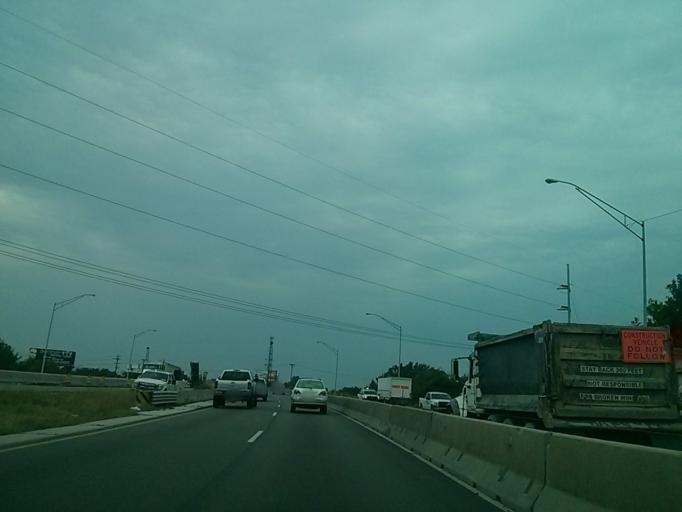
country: US
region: Oklahoma
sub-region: Tulsa County
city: Tulsa
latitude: 36.1627
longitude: -95.9111
